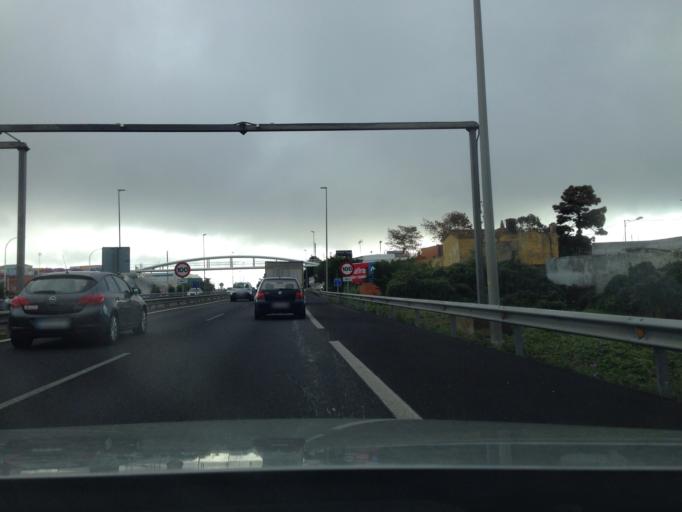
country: ES
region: Canary Islands
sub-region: Provincia de Santa Cruz de Tenerife
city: La Laguna
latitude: 28.4903
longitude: -16.3548
